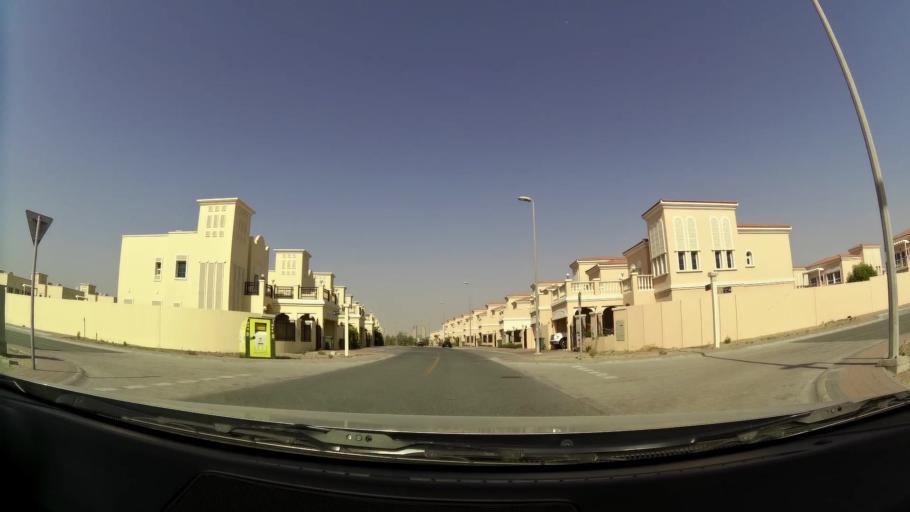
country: AE
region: Dubai
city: Dubai
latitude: 25.0718
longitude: 55.2126
